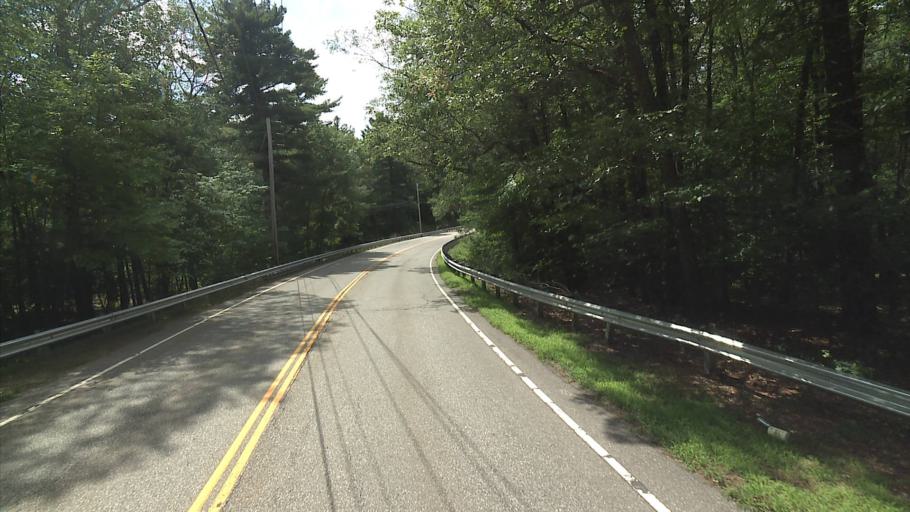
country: US
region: Massachusetts
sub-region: Hampden County
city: Holland
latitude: 41.9885
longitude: -72.1625
